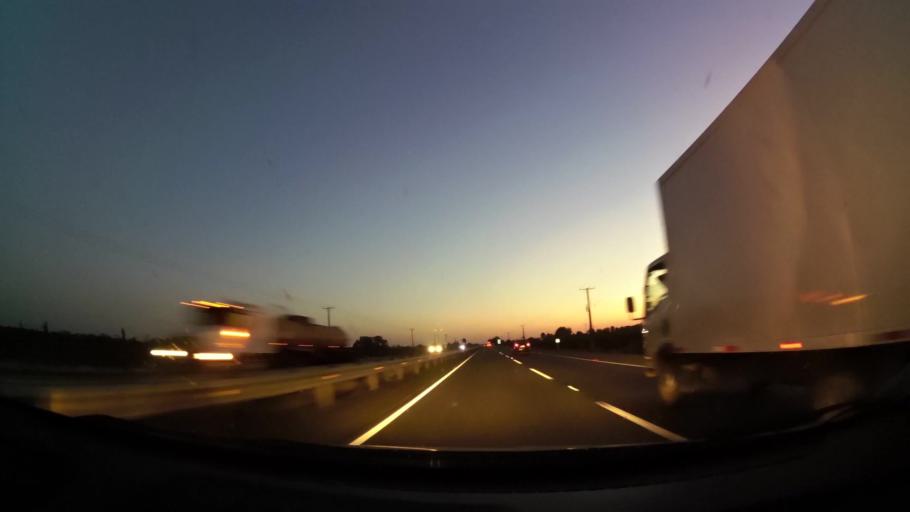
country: CL
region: Biobio
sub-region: Provincia de Nuble
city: San Carlos
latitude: -36.3122
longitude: -71.8330
